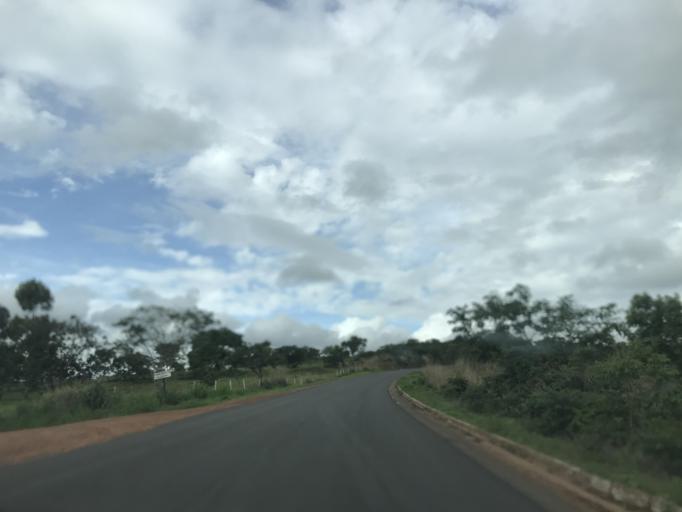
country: BR
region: Goias
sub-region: Bela Vista De Goias
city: Bela Vista de Goias
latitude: -17.0370
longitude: -48.6612
